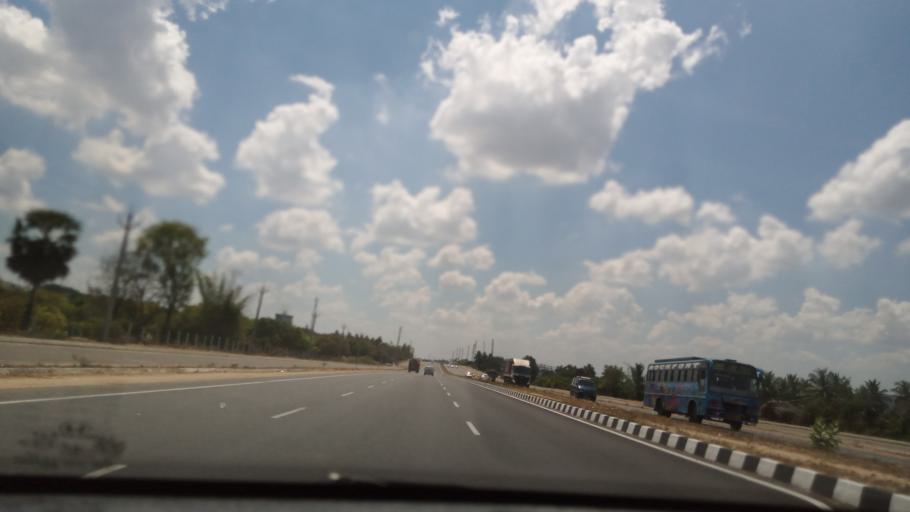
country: IN
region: Andhra Pradesh
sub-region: Chittoor
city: Pakala
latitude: 13.4653
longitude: 79.1757
